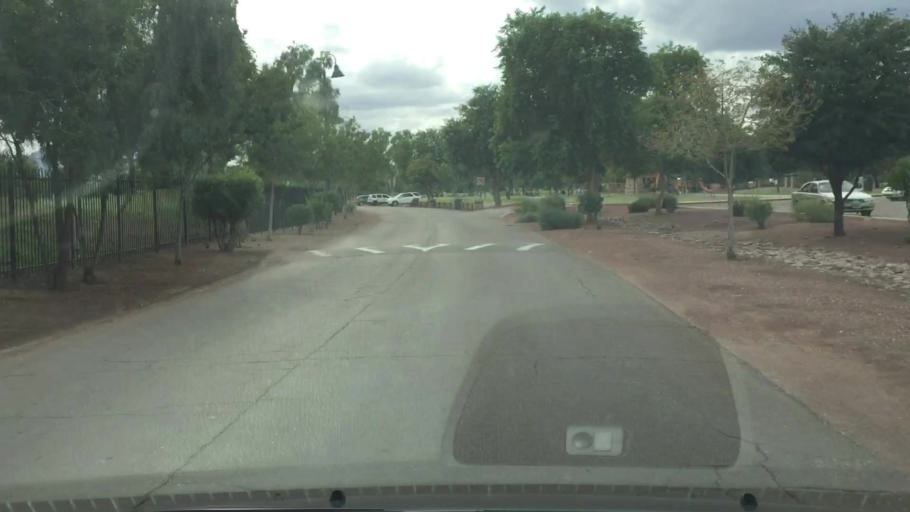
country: US
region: Arizona
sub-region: Maricopa County
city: Laveen
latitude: 33.3726
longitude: -112.1363
